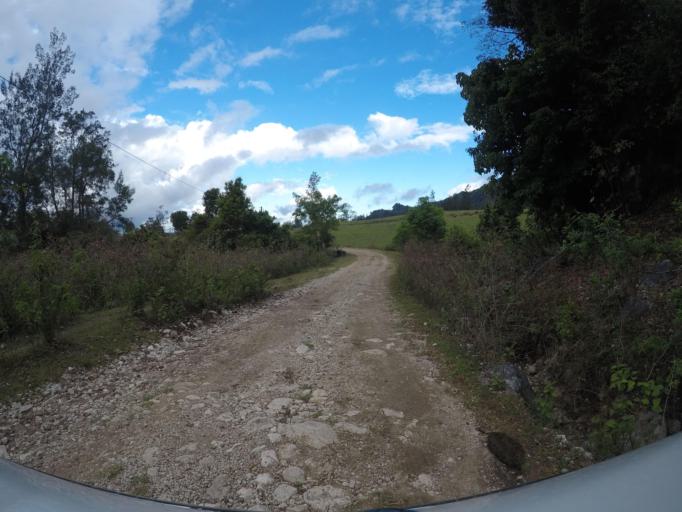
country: TL
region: Baucau
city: Venilale
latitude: -8.6807
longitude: 126.6393
